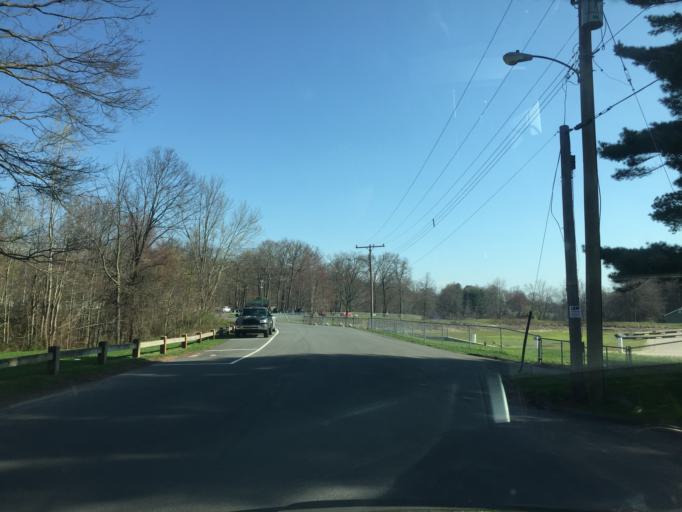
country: US
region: Connecticut
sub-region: Hartford County
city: Wethersfield
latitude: 41.6921
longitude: -72.6665
